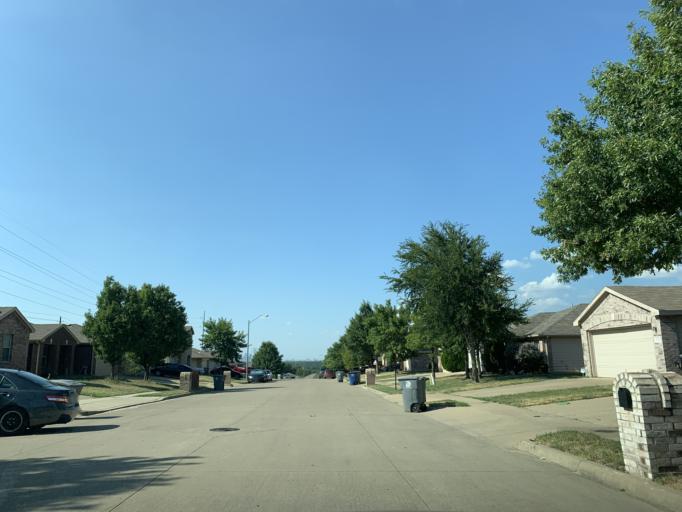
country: US
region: Texas
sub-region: Dallas County
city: Hutchins
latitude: 32.6660
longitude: -96.7700
